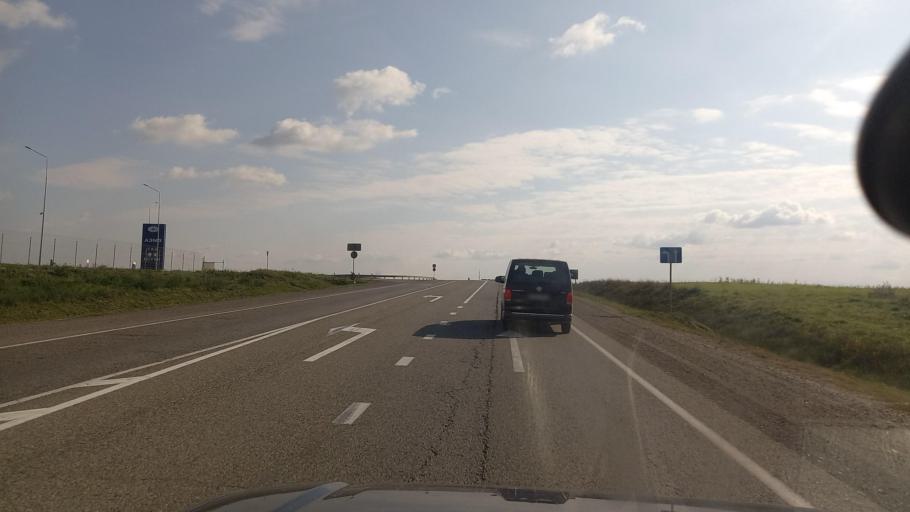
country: RU
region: Krasnodarskiy
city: Abinsk
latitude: 44.8740
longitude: 38.1138
